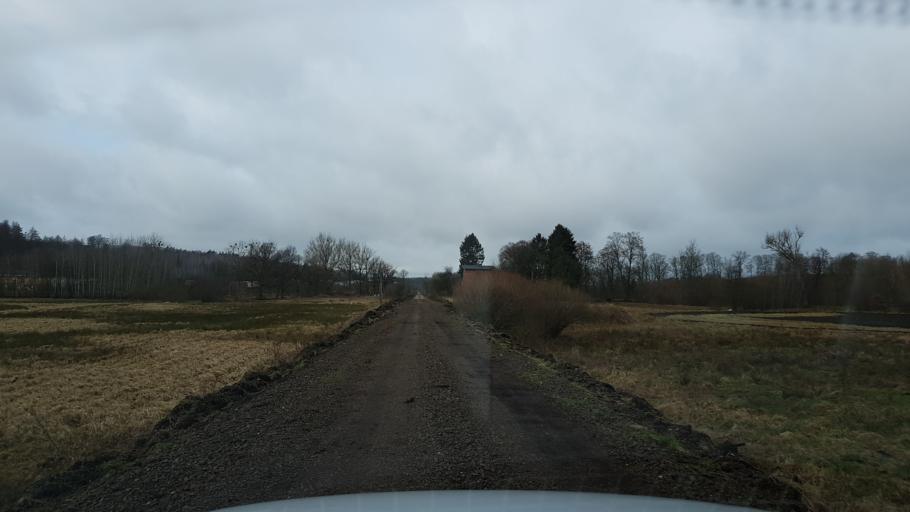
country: PL
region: West Pomeranian Voivodeship
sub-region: Powiat swidwinski
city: Polczyn-Zdroj
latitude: 53.7884
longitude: 16.0459
